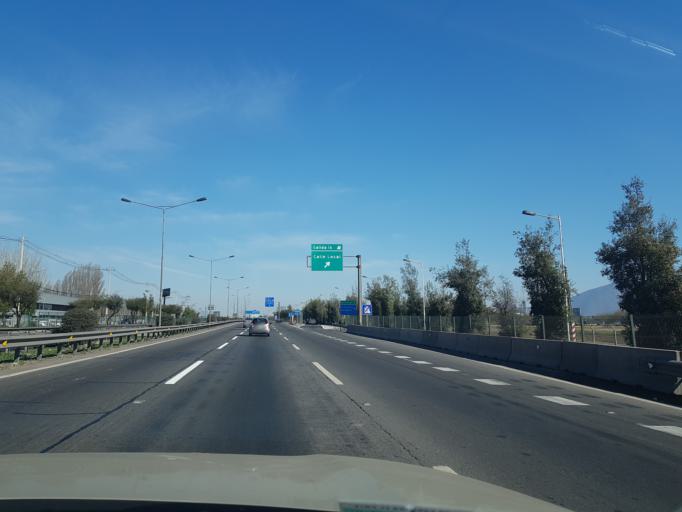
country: CL
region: Santiago Metropolitan
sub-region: Provincia de Santiago
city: Lo Prado
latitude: -33.4093
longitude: -70.7824
